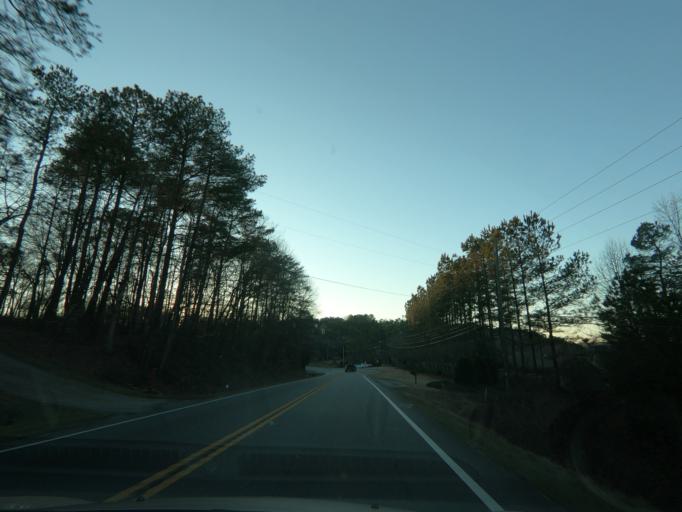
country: US
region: Georgia
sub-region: Cherokee County
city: Ball Ground
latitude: 34.2991
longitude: -84.2476
